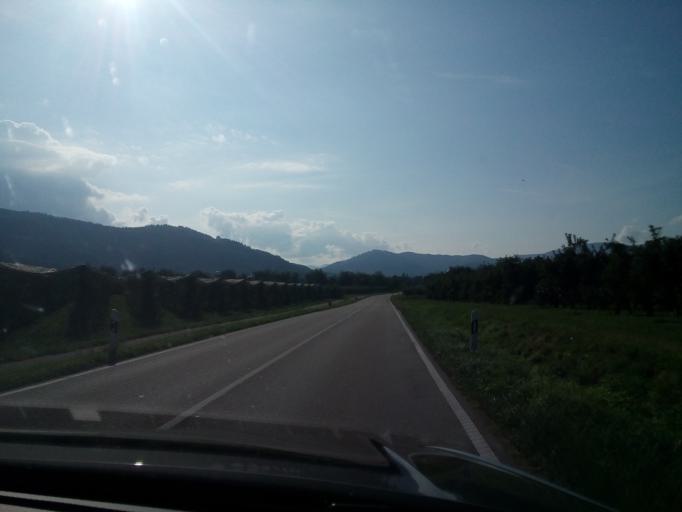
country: DE
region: Baden-Wuerttemberg
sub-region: Freiburg Region
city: Haslach
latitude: 48.5468
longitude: 8.0633
